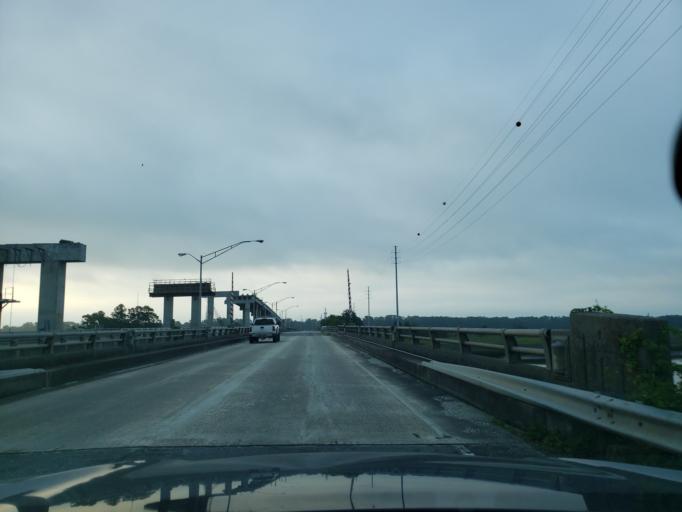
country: US
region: Georgia
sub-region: Chatham County
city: Thunderbolt
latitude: 32.0625
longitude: -81.0307
